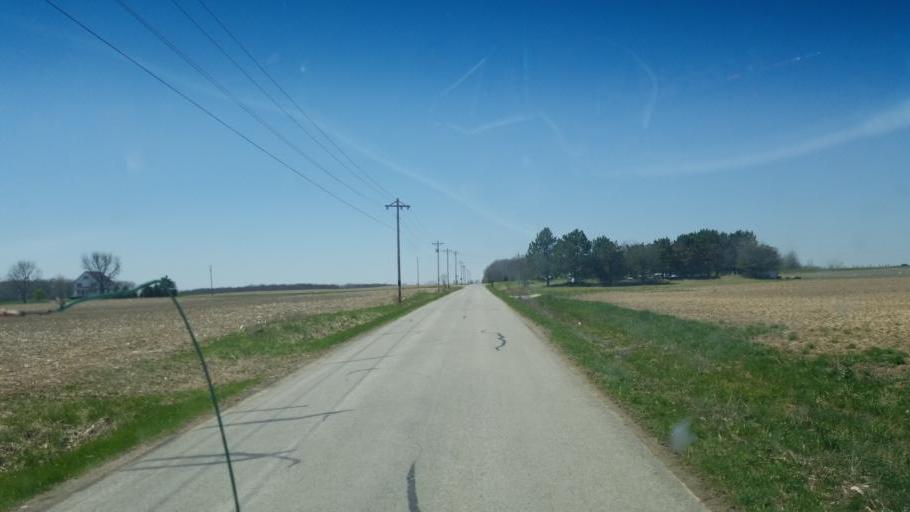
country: US
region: Ohio
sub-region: Huron County
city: Greenwich
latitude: 41.0938
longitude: -82.5106
